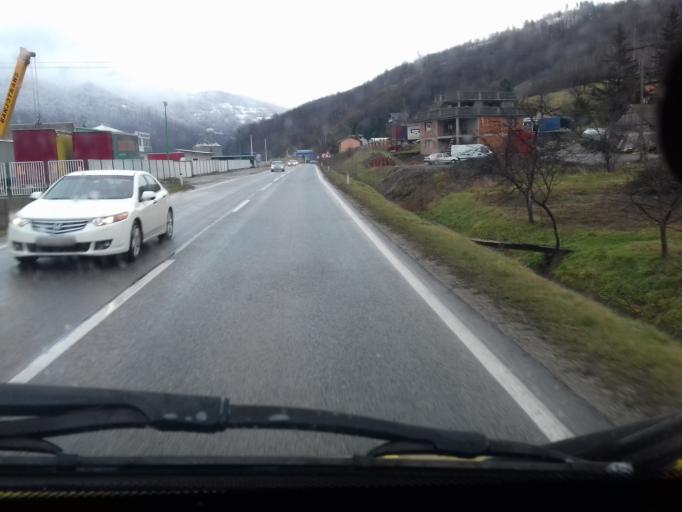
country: BA
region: Federation of Bosnia and Herzegovina
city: Zeljezno Polje
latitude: 44.3799
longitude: 17.9909
